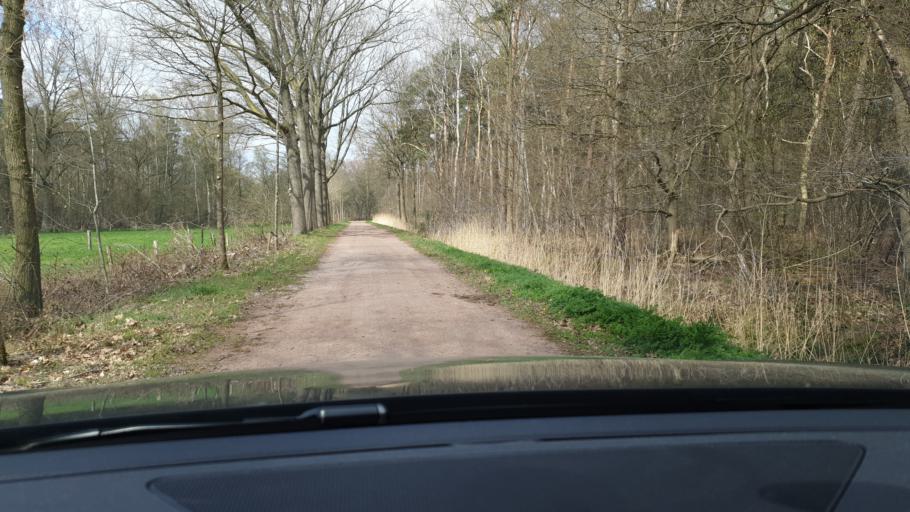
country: NL
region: North Brabant
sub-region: Gemeente Best
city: Best
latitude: 51.5353
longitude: 5.3611
